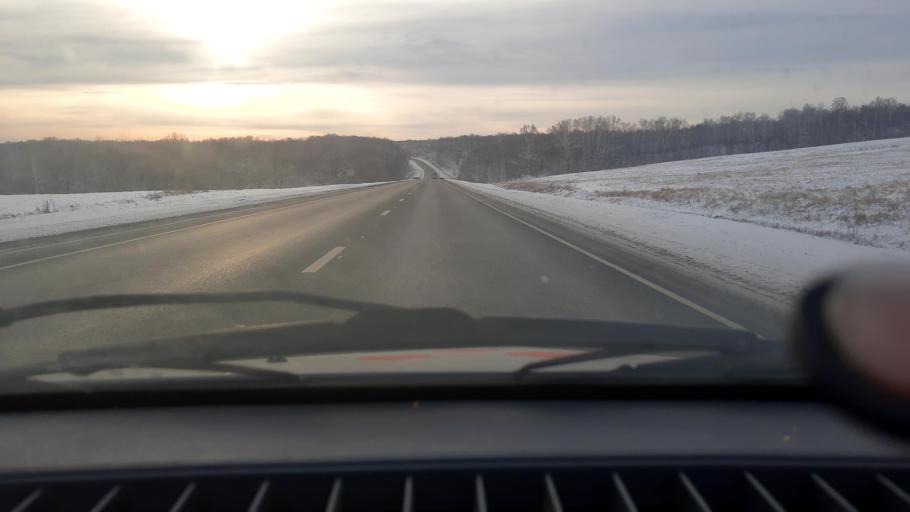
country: RU
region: Bashkortostan
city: Avdon
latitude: 54.8299
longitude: 55.7253
